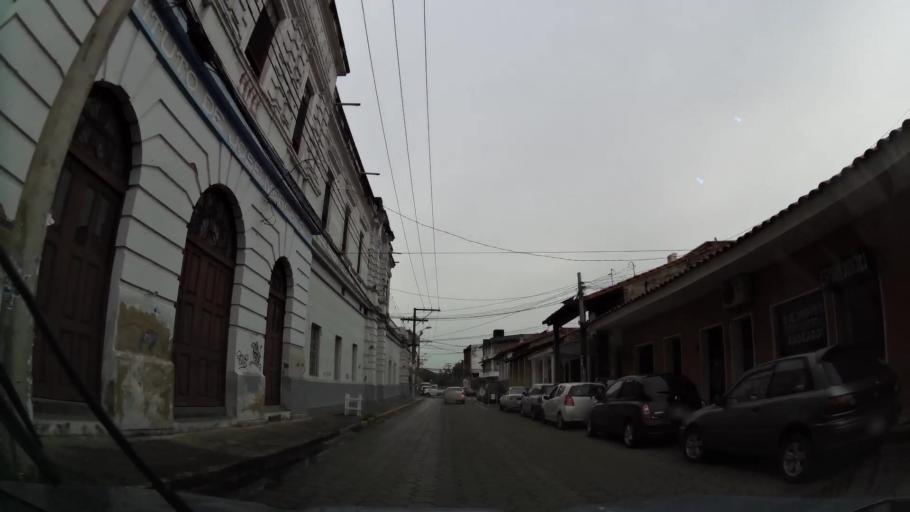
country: BO
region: Santa Cruz
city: Santa Cruz de la Sierra
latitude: -17.7890
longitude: -63.1814
